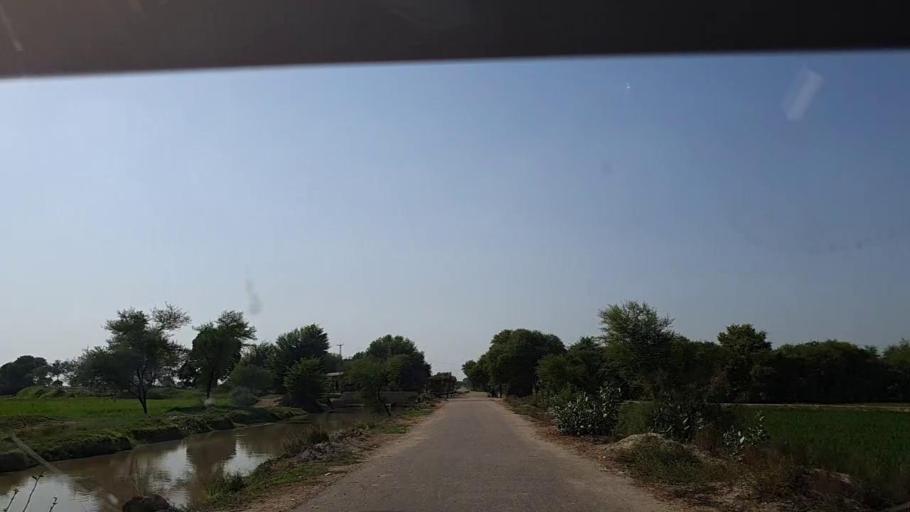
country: PK
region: Sindh
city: Tangwani
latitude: 28.2062
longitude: 69.0317
